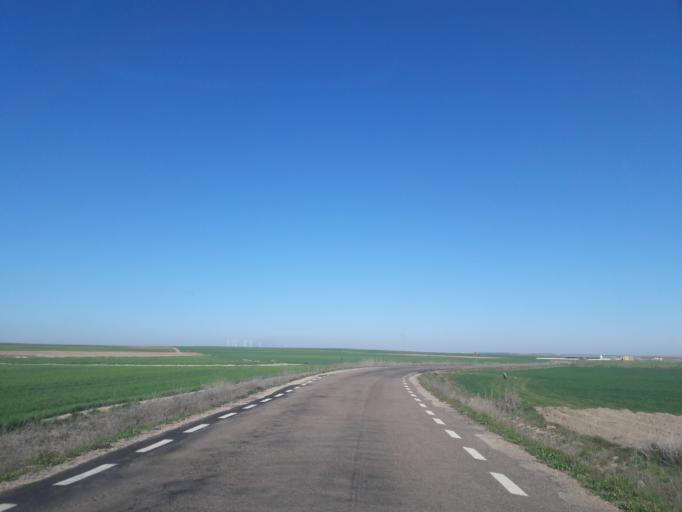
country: ES
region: Castille and Leon
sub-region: Provincia de Salamanca
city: Tordillos
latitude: 40.8616
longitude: -5.3663
